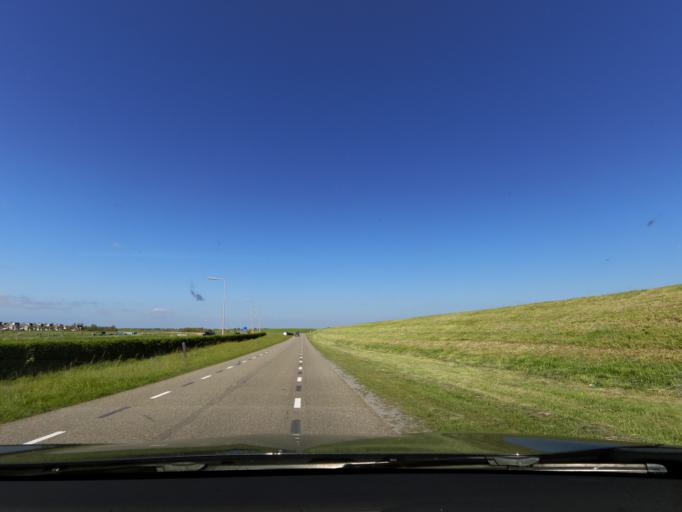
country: NL
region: South Holland
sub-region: Gemeente Goeree-Overflakkee
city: Ouddorp
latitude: 51.7996
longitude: 3.9405
